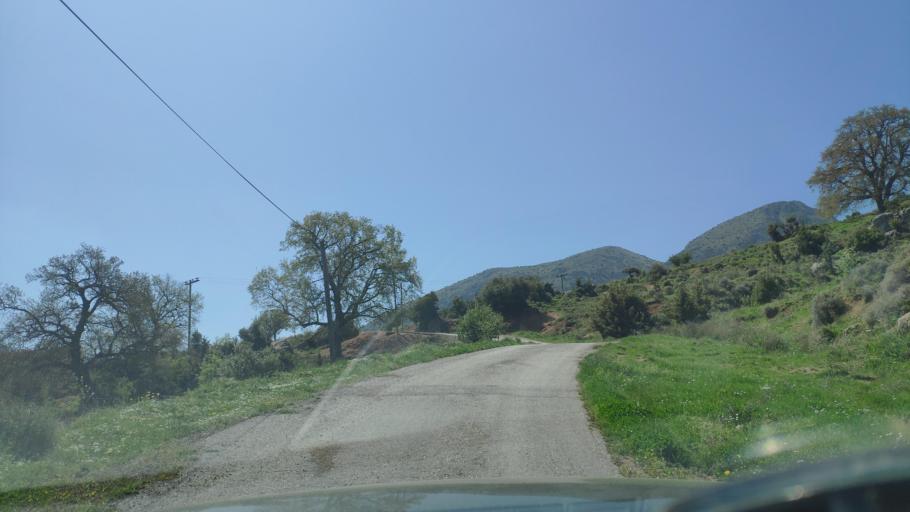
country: GR
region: West Greece
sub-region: Nomos Achaias
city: Akrata
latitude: 38.0796
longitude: 22.3230
